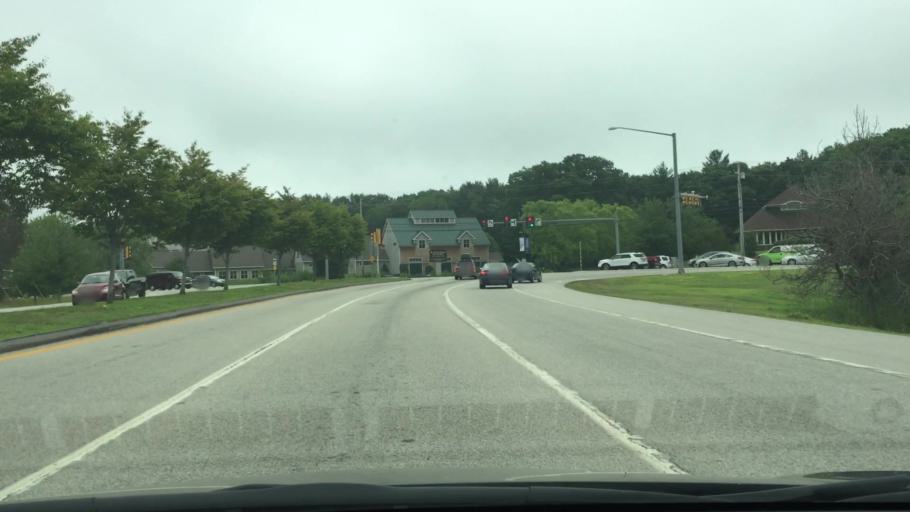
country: US
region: Maine
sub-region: York County
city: York Harbor
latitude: 43.1549
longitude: -70.6600
